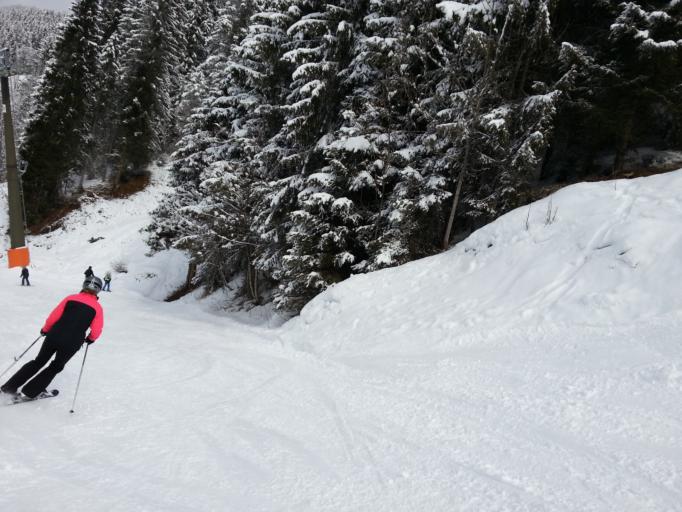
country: AT
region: Salzburg
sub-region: Politischer Bezirk Sankt Johann im Pongau
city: Kleinarl
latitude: 47.2815
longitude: 13.3211
